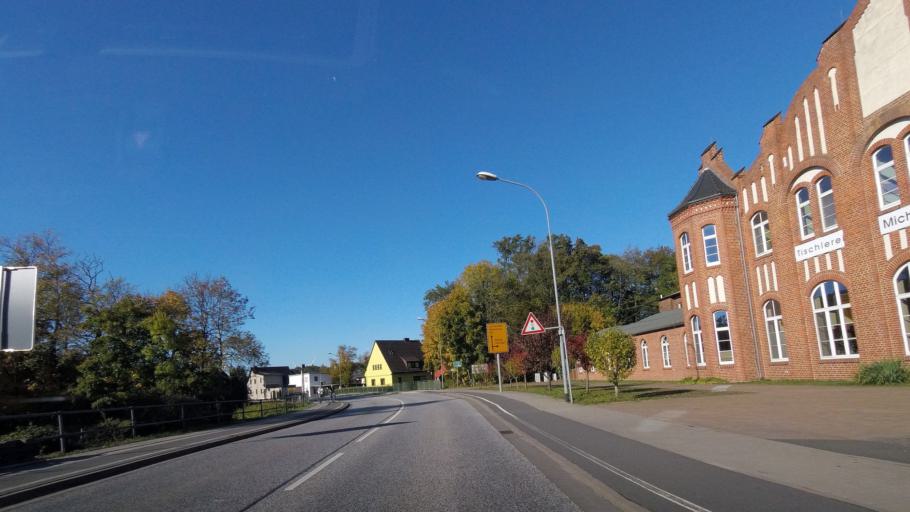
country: DE
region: Saxony-Anhalt
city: Muhlanger
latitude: 51.8542
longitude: 12.7481
